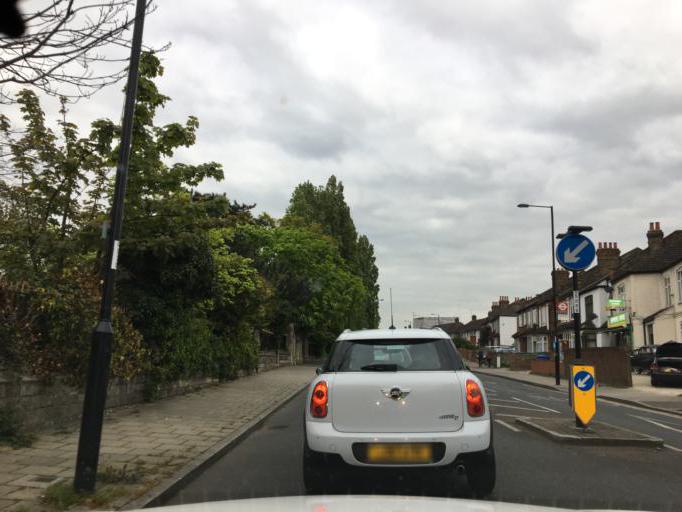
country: GB
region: England
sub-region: Greater London
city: Blackheath
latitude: 51.4376
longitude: 0.0060
